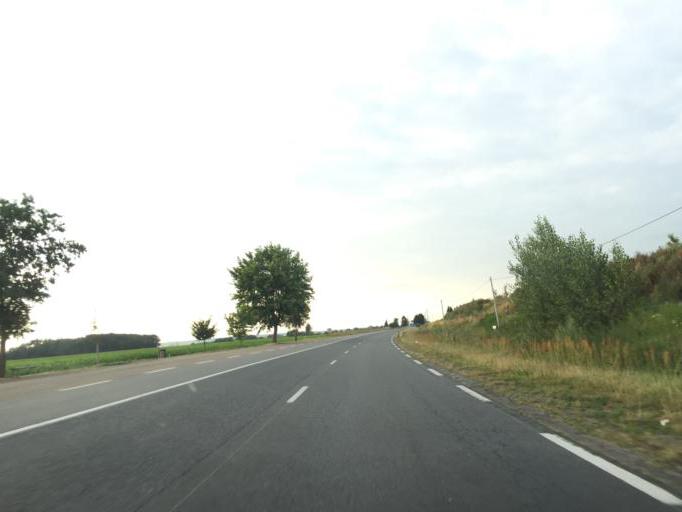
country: FR
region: Auvergne
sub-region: Departement de l'Allier
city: Varennes-sur-Allier
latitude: 46.3695
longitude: 3.3641
